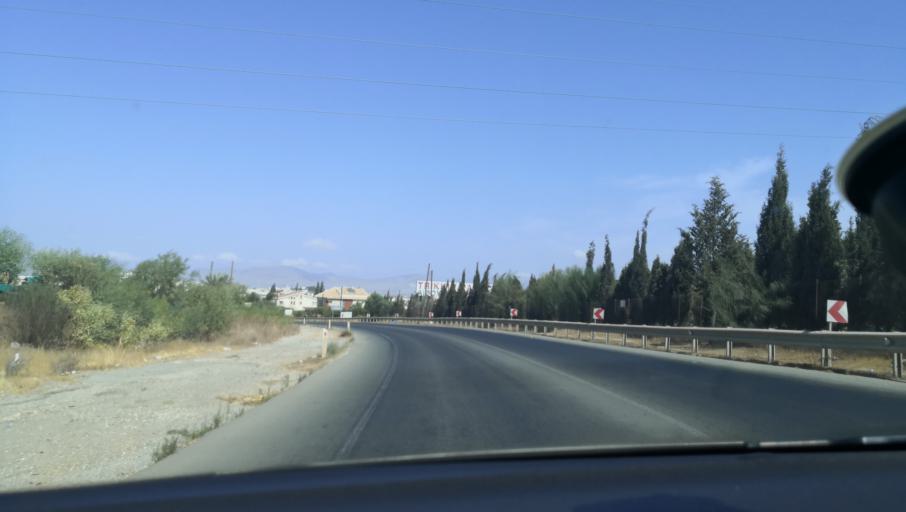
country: CY
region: Lefkosia
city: Kato Deftera
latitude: 35.0980
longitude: 33.2871
